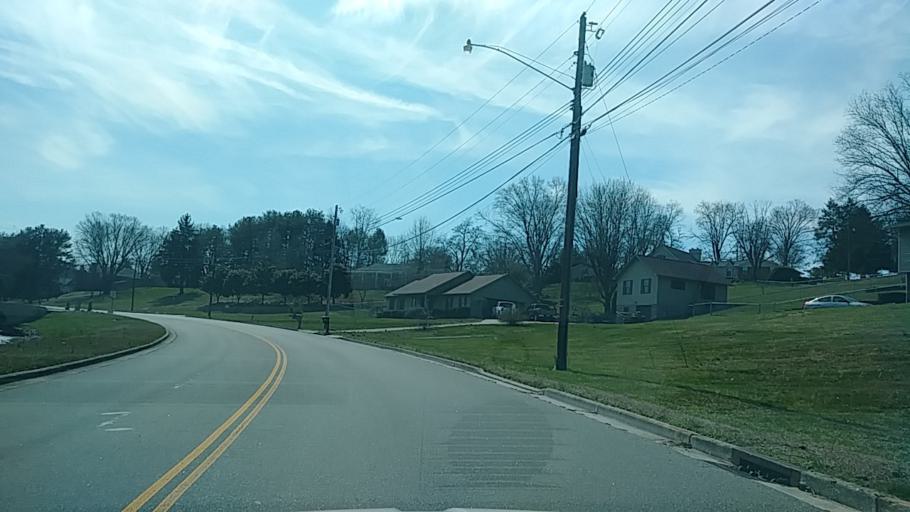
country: US
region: Tennessee
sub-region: Hamblen County
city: Morristown
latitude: 36.2198
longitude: -83.3212
